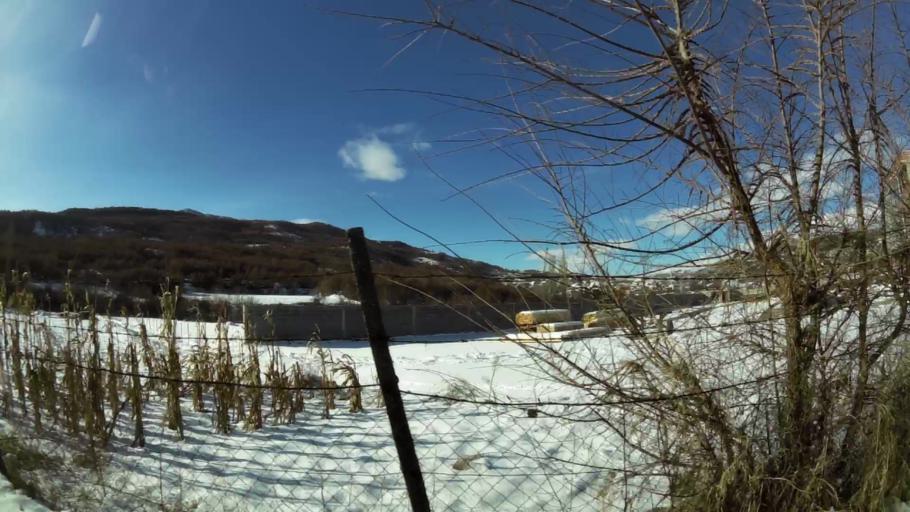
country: MK
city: Ljubin
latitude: 41.9868
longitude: 21.2960
